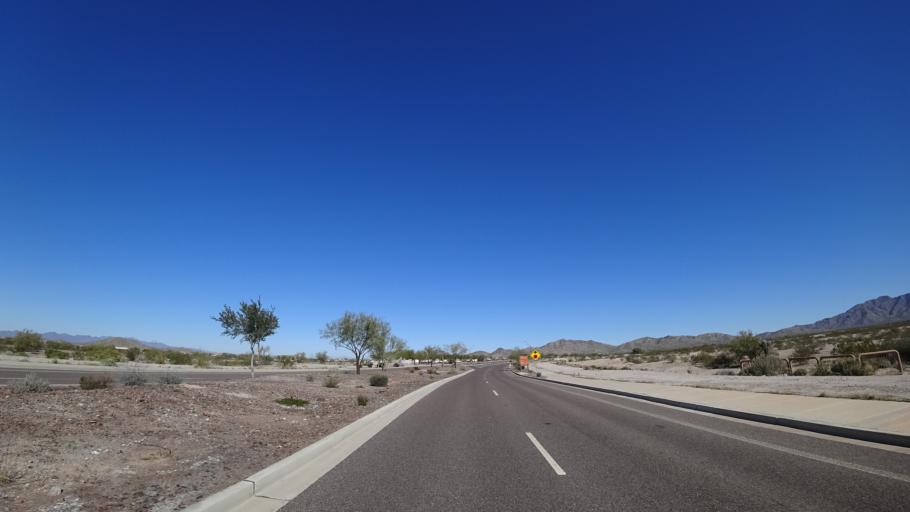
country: US
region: Arizona
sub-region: Maricopa County
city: Goodyear
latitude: 33.3165
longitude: -112.4326
